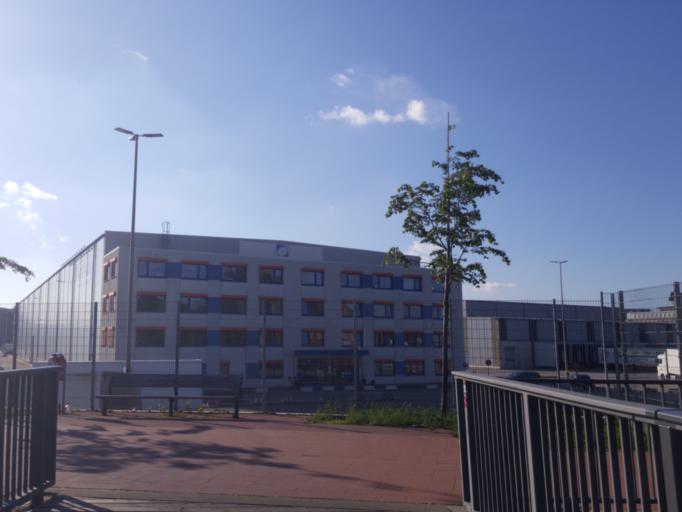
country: DE
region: Hamburg
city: Hammerbrook
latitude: 53.5401
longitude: 10.0243
